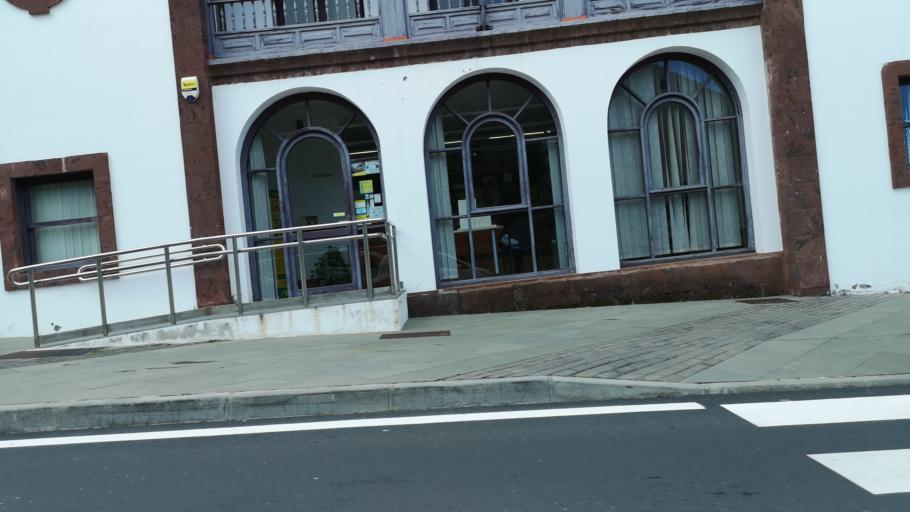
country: ES
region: Canary Islands
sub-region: Provincia de Santa Cruz de Tenerife
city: Hermigua
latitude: 28.1628
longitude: -17.1984
